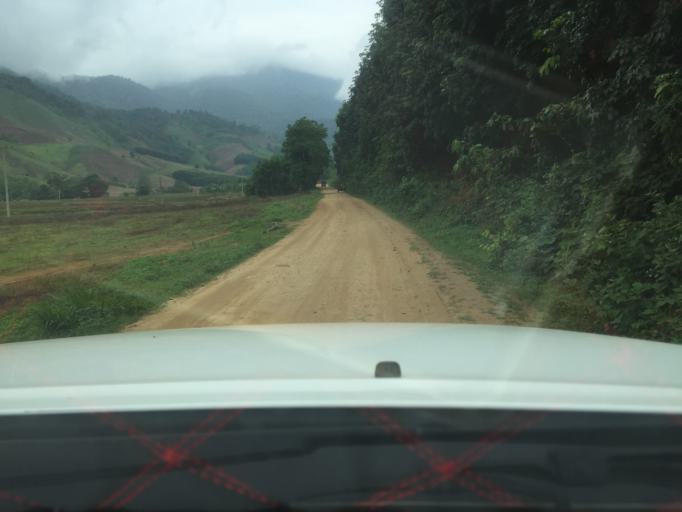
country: TH
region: Phayao
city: Phu Sang
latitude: 19.7420
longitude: 100.4452
